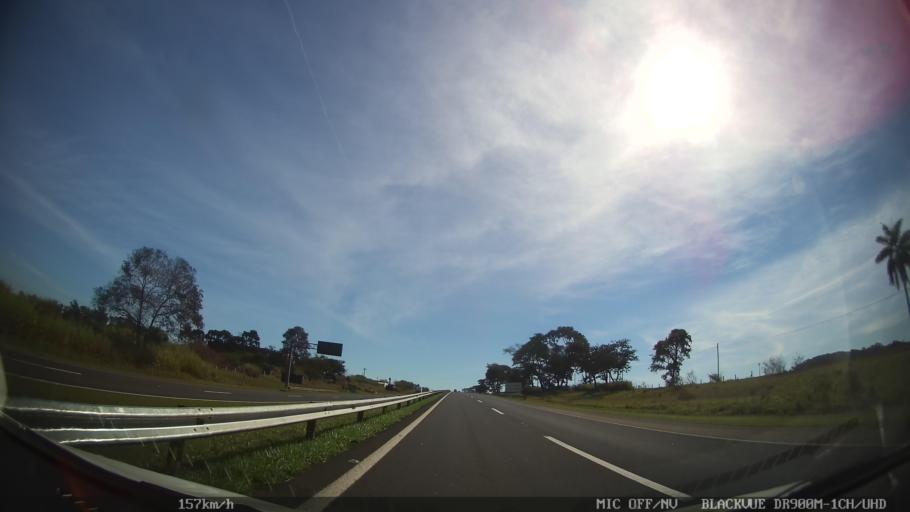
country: BR
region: Sao Paulo
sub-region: Pirassununga
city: Pirassununga
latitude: -21.9913
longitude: -47.4480
